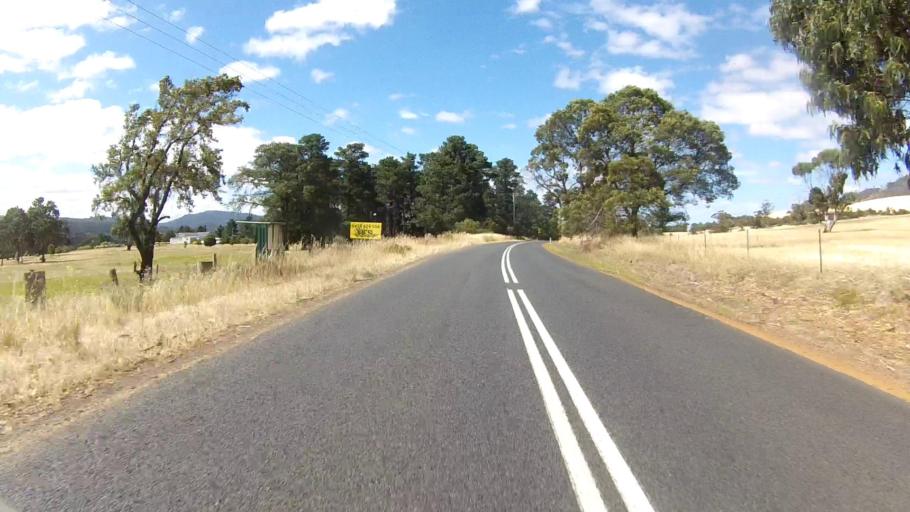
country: AU
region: Tasmania
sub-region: Sorell
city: Sorell
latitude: -42.6124
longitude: 147.4272
